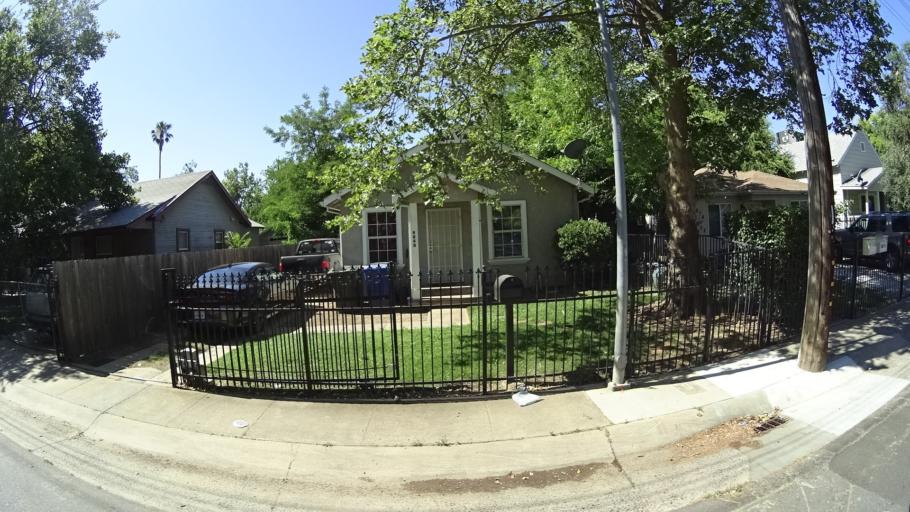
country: US
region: California
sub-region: Sacramento County
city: Parkway
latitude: 38.5422
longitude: -121.4598
